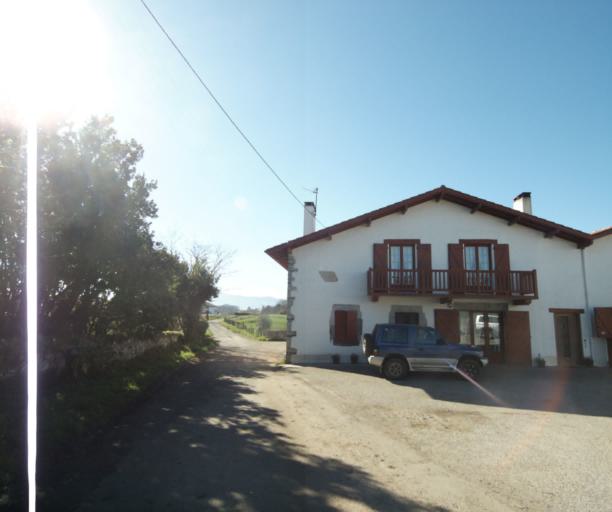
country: FR
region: Aquitaine
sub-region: Departement des Pyrenees-Atlantiques
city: Urrugne
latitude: 43.3698
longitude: -1.7273
